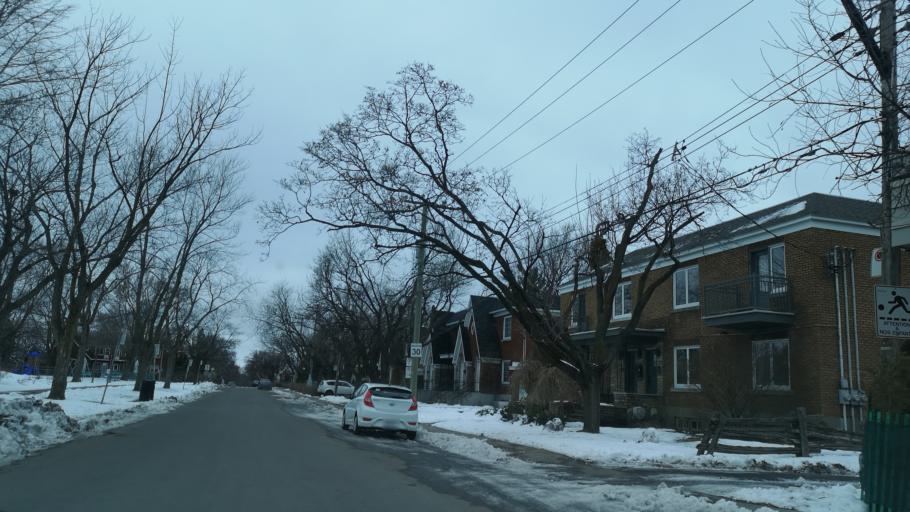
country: CA
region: Quebec
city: Saint-Laurent
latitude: 45.5083
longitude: -73.6801
